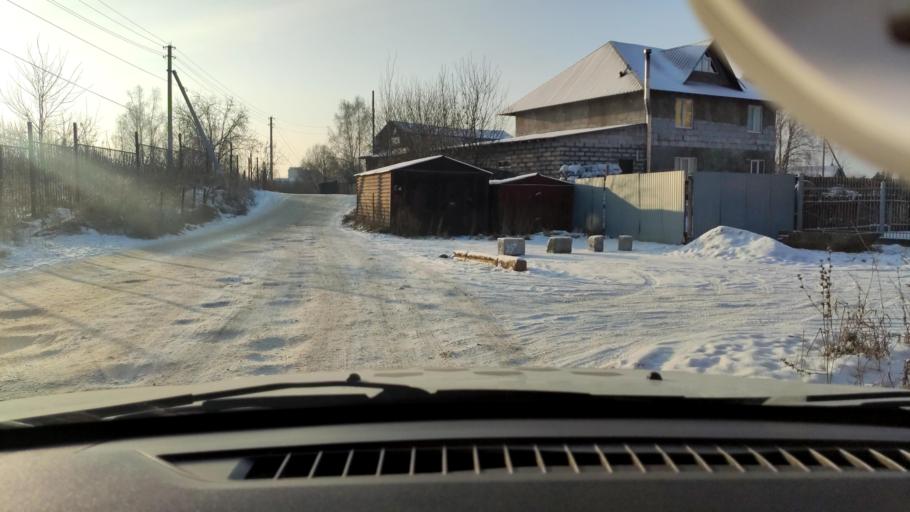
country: RU
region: Perm
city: Kondratovo
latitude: 57.9593
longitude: 56.1752
